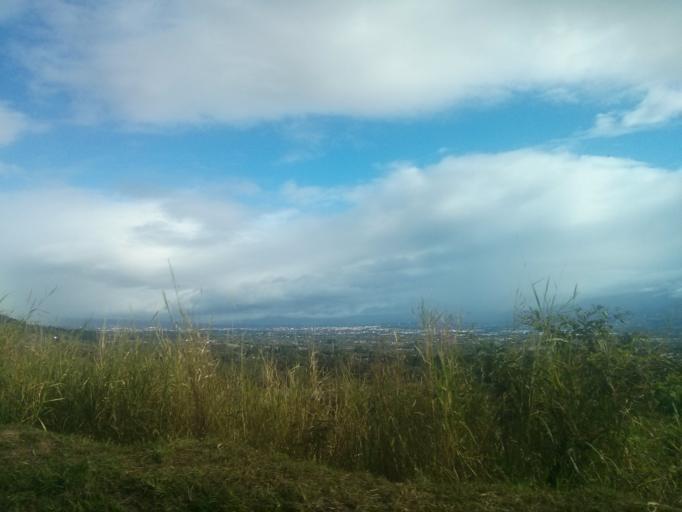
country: CR
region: Alajuela
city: Sabanilla
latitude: 10.0538
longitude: -84.2025
